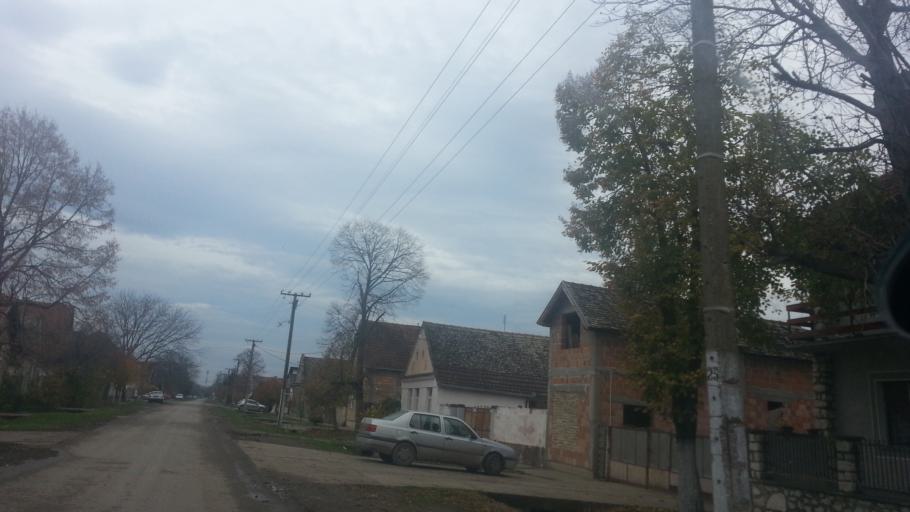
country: RS
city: Golubinci
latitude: 44.9861
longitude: 20.0748
